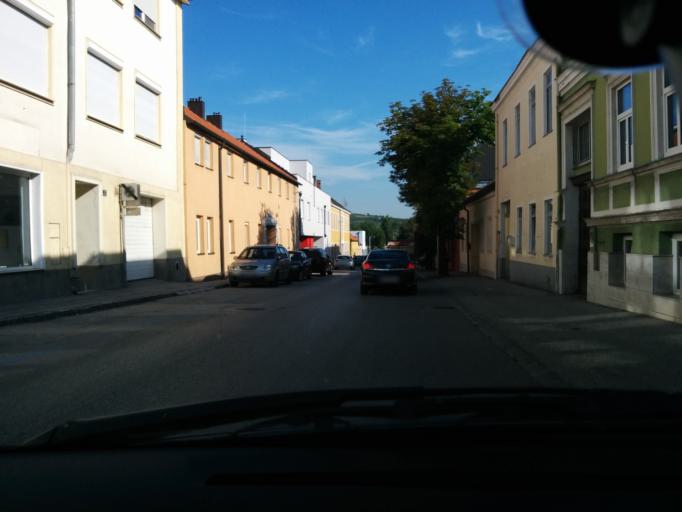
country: AT
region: Lower Austria
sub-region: Politischer Bezirk Modling
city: Guntramsdorf
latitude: 48.0500
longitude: 16.3118
